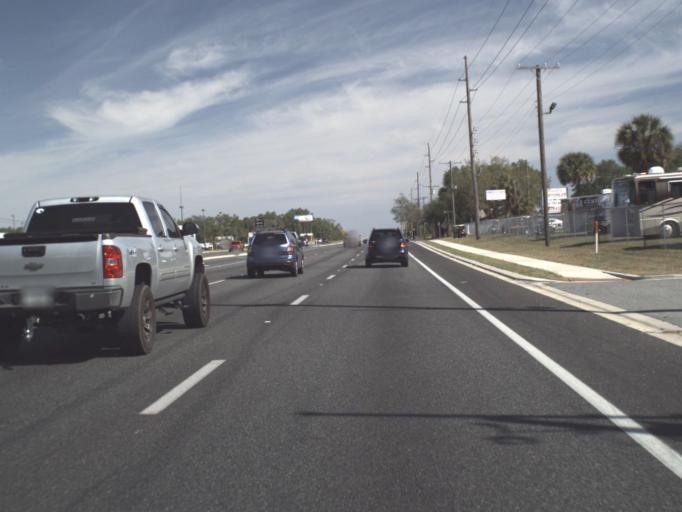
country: US
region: Florida
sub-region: Lake County
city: Fruitland Park
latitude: 28.8784
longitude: -81.9063
